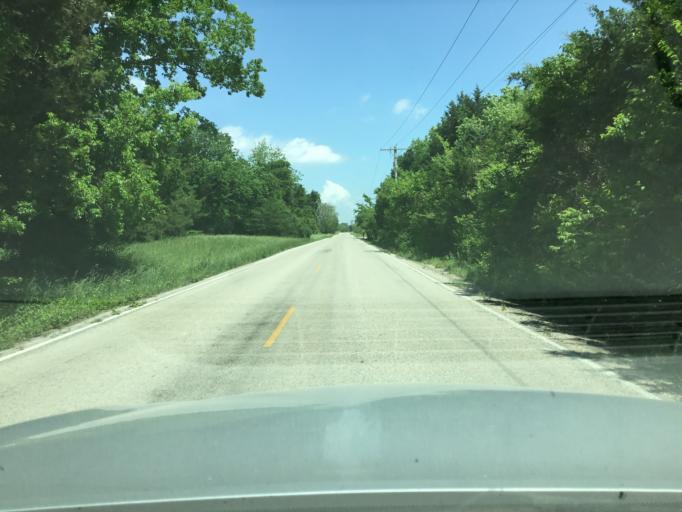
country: US
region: Kansas
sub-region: Labette County
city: Parsons
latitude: 37.3418
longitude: -95.3039
